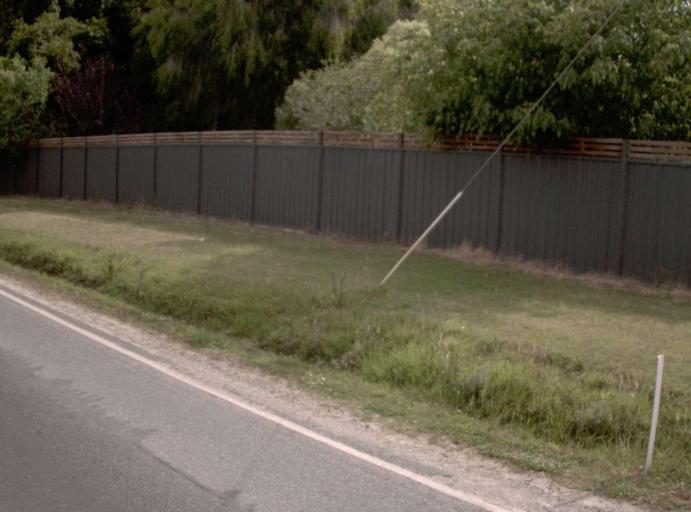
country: AU
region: Victoria
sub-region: Casey
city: Junction Village
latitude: -38.1540
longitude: 145.3200
